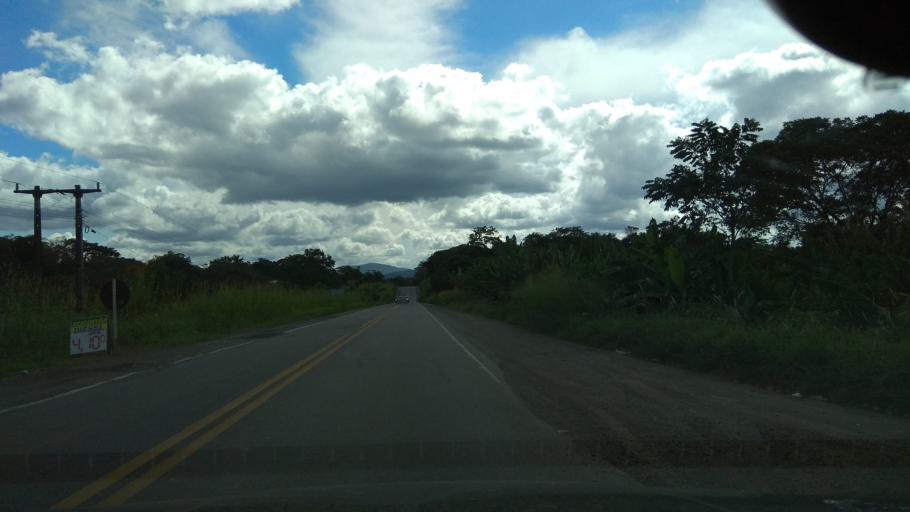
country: BR
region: Bahia
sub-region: Itajuipe
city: Itajuipe
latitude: -14.7264
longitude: -39.3473
